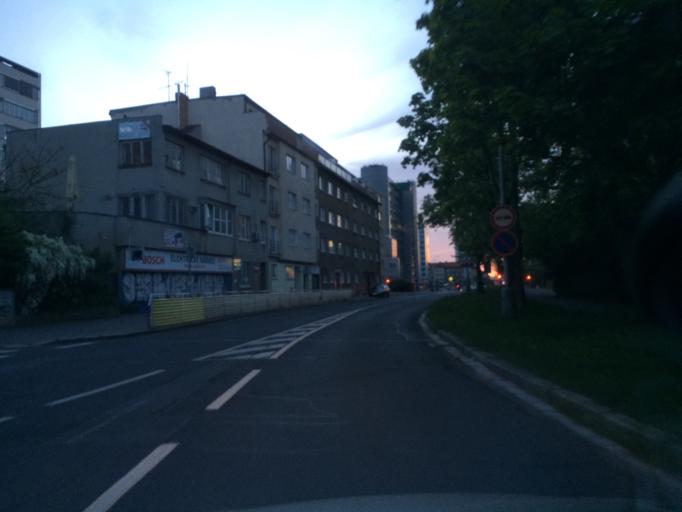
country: CZ
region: Praha
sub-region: Praha 4
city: Hodkovicky
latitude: 50.0430
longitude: 14.4526
